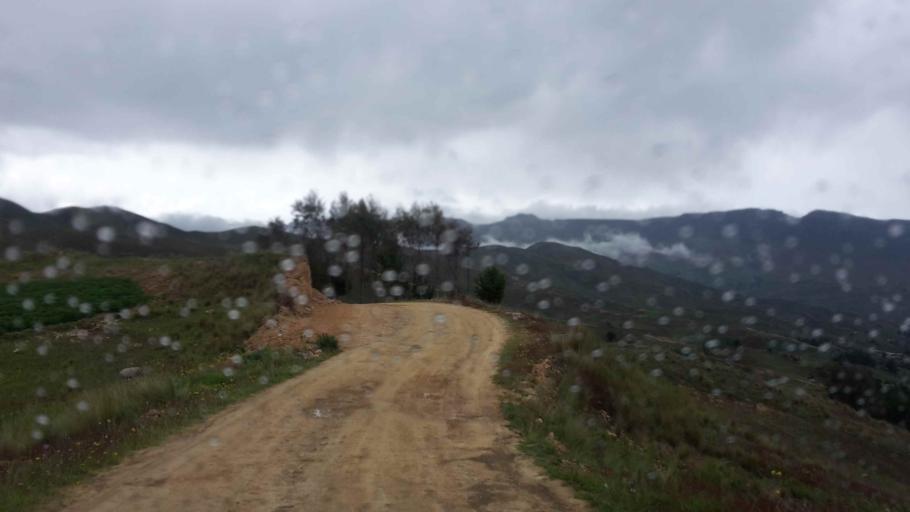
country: BO
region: Cochabamba
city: Cochabamba
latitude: -17.1395
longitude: -66.1048
